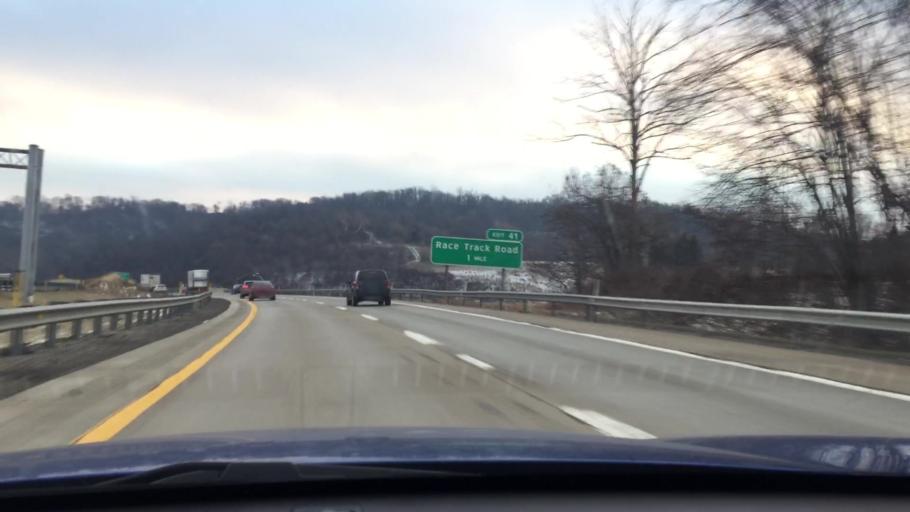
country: US
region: Pennsylvania
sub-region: Washington County
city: McGovern
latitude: 40.2111
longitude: -80.2285
